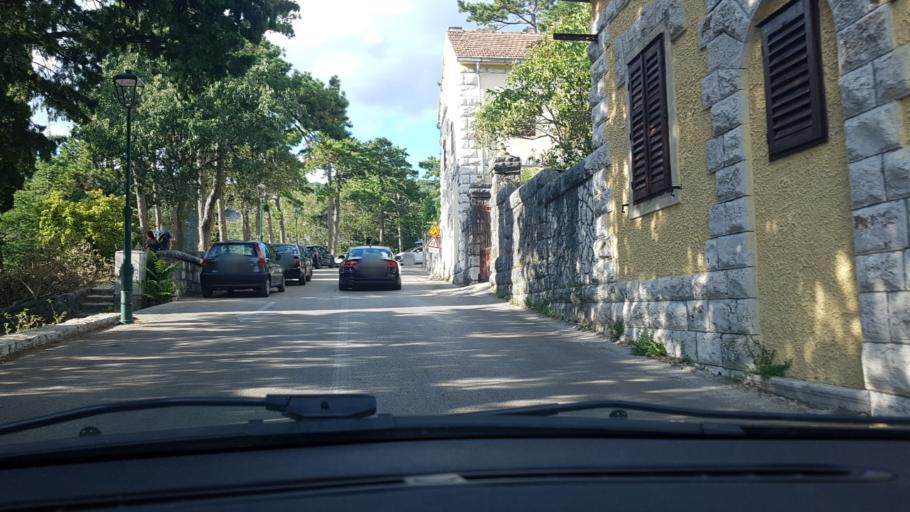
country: HR
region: Splitsko-Dalmatinska
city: Imotski
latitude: 43.4480
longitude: 17.2107
